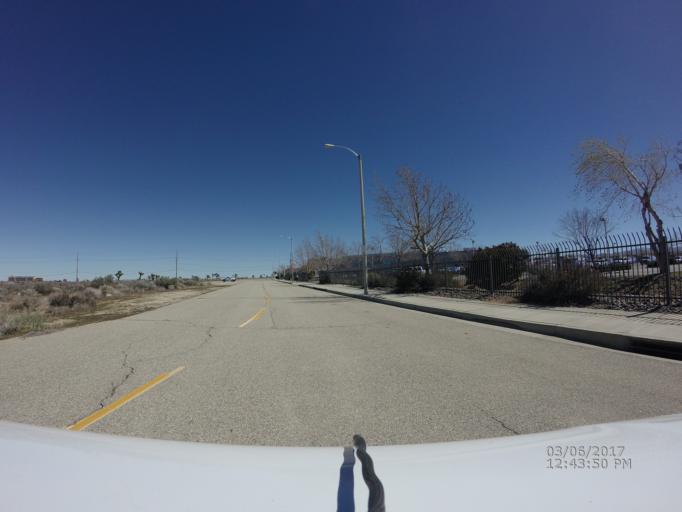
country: US
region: California
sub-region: Los Angeles County
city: Desert View Highlands
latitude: 34.6385
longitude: -118.1497
